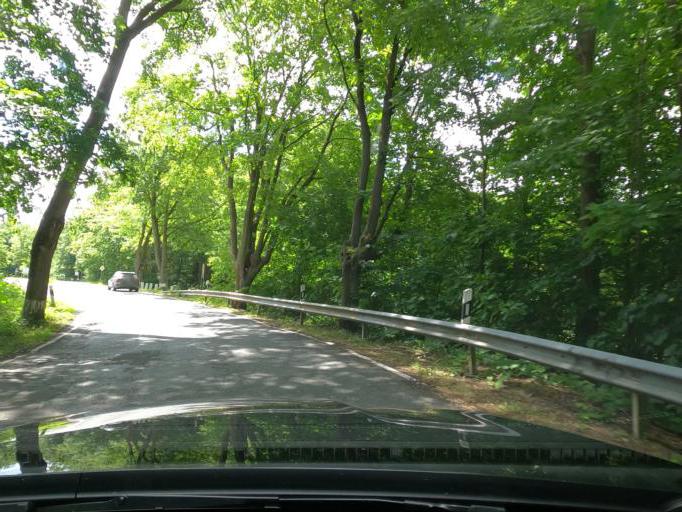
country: DE
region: Lower Saxony
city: Elbe
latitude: 52.1215
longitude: 10.2931
